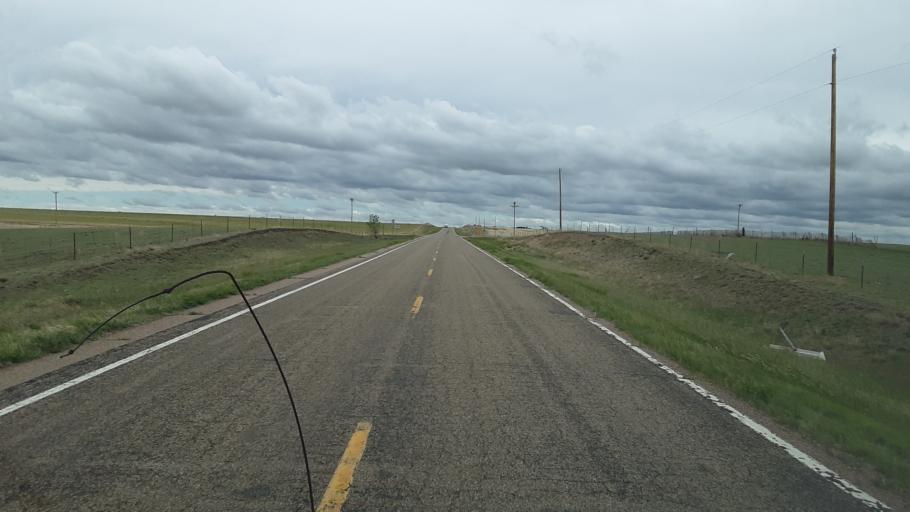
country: US
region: Colorado
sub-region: Lincoln County
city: Limon
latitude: 38.8384
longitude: -103.8675
